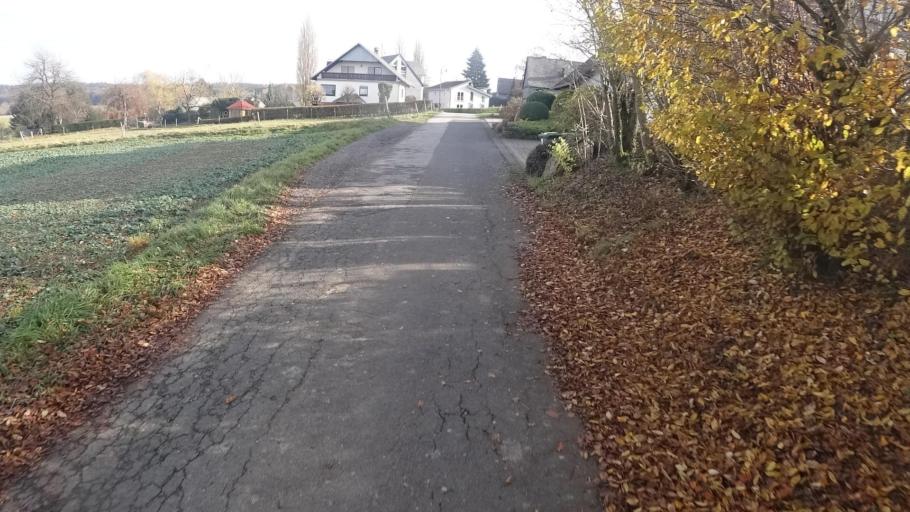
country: DE
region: Rheinland-Pfalz
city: Lingerhahn
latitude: 50.0959
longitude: 7.5611
